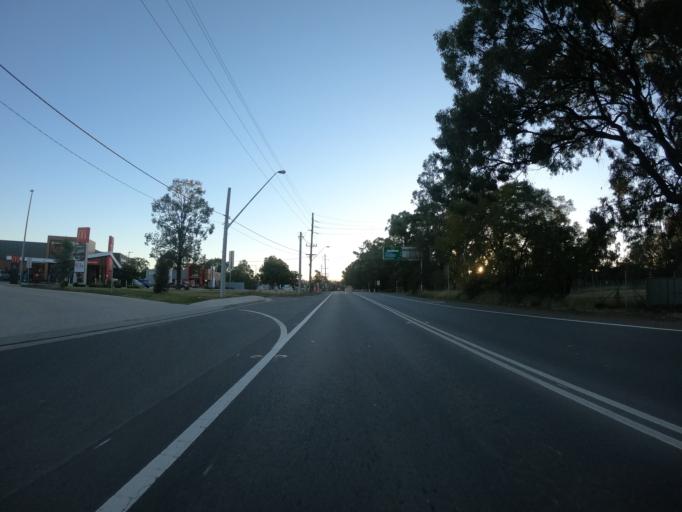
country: AU
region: New South Wales
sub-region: Hawkesbury
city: South Windsor
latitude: -33.6388
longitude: 150.7850
